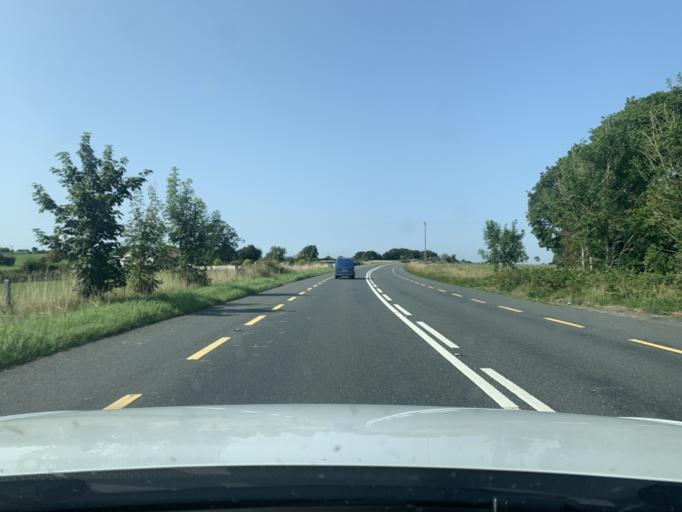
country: IE
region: Leinster
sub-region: An Iarmhi
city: Athlone
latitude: 53.5112
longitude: -8.0515
